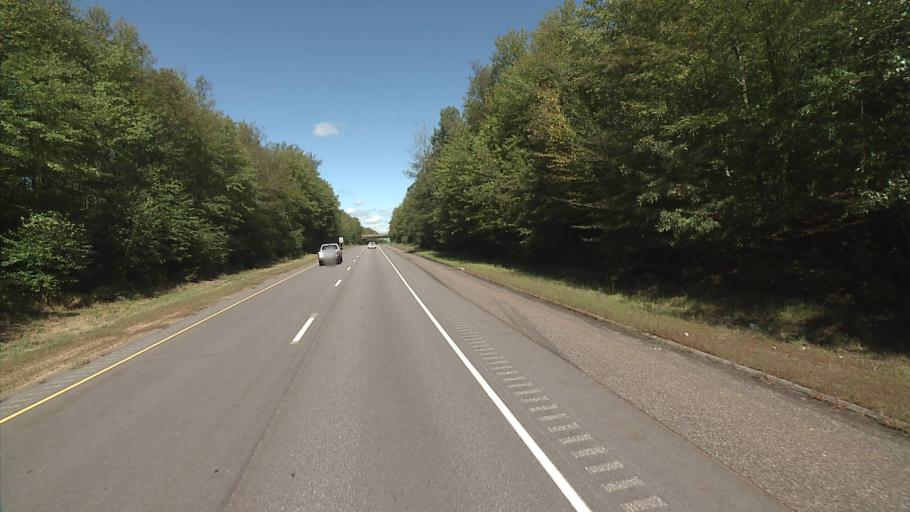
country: US
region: Connecticut
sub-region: New London County
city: Colchester
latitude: 41.5360
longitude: -72.3107
